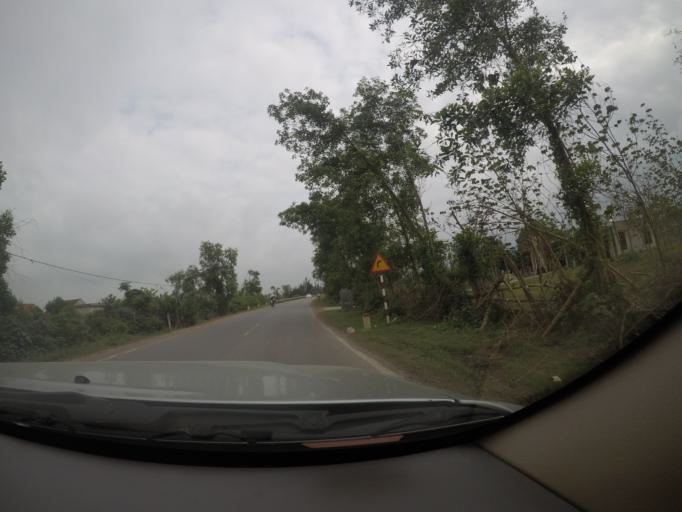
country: VN
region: Quang Binh
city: Quan Hau
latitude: 17.4230
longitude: 106.5948
